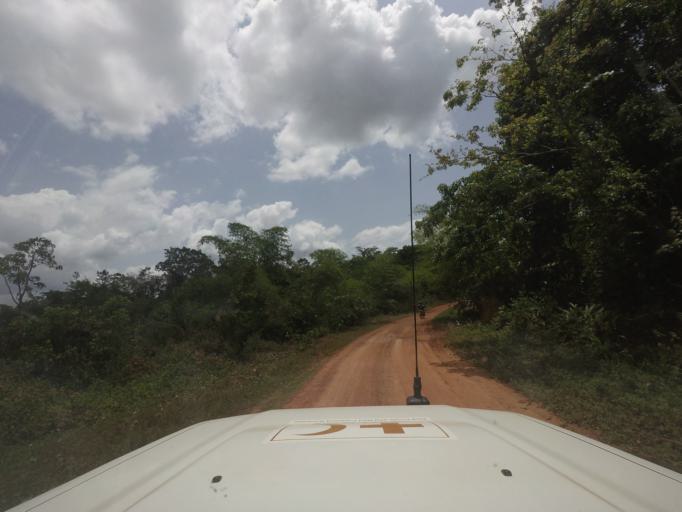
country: LR
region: Bong
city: Gbarnga
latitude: 7.1558
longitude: -9.2142
